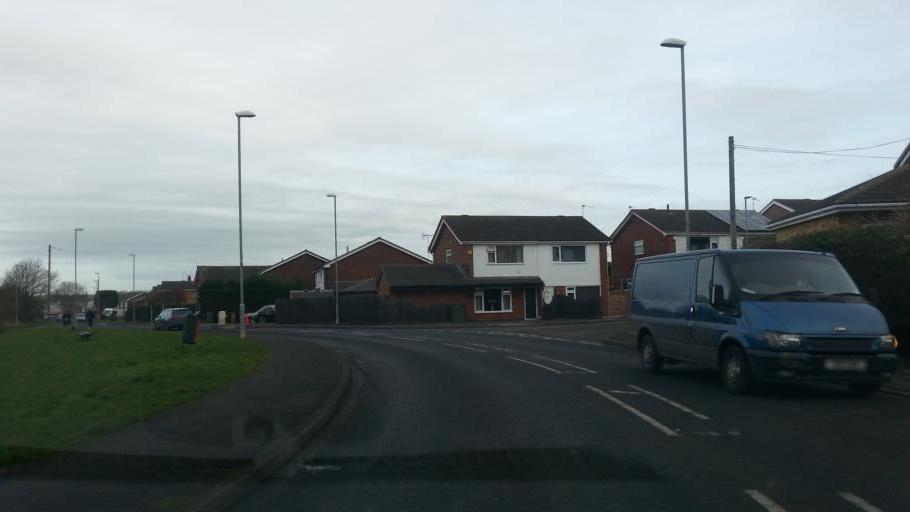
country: GB
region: England
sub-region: Leicestershire
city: Melton Mowbray
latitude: 52.7550
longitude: -0.8962
